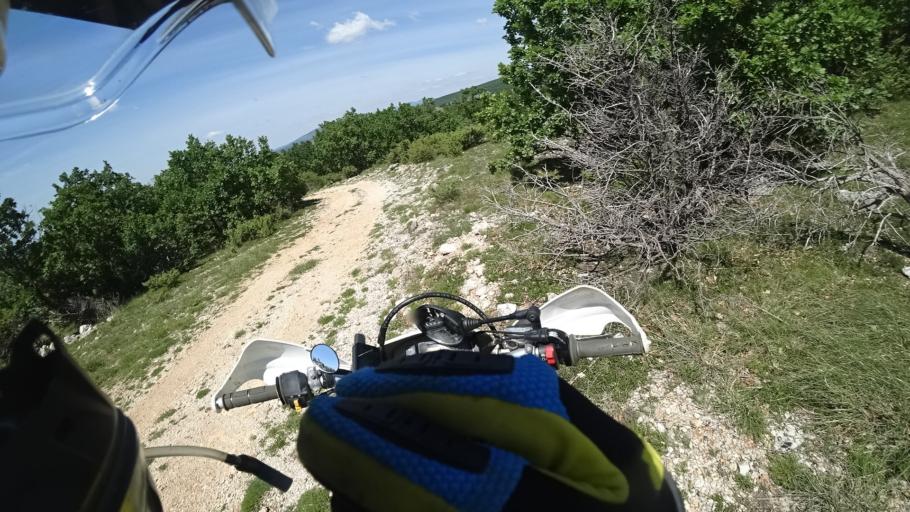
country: HR
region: Sibensko-Kniniska
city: Knin
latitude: 44.0315
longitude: 16.2824
